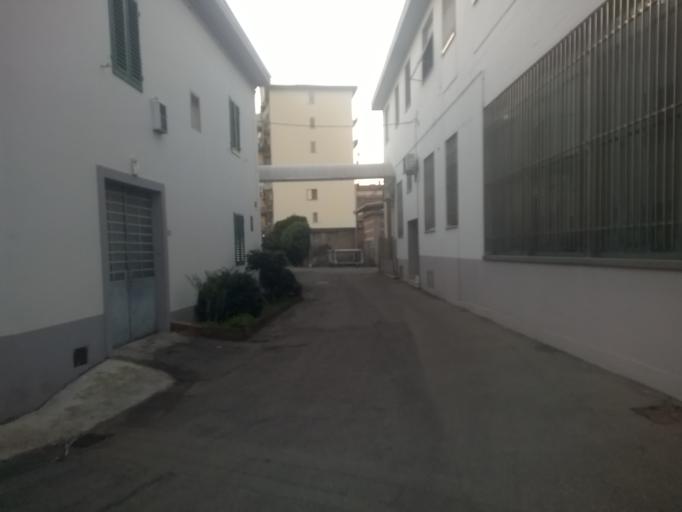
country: IT
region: Tuscany
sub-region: Provincia di Prato
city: Prato
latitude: 43.8703
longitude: 11.1012
